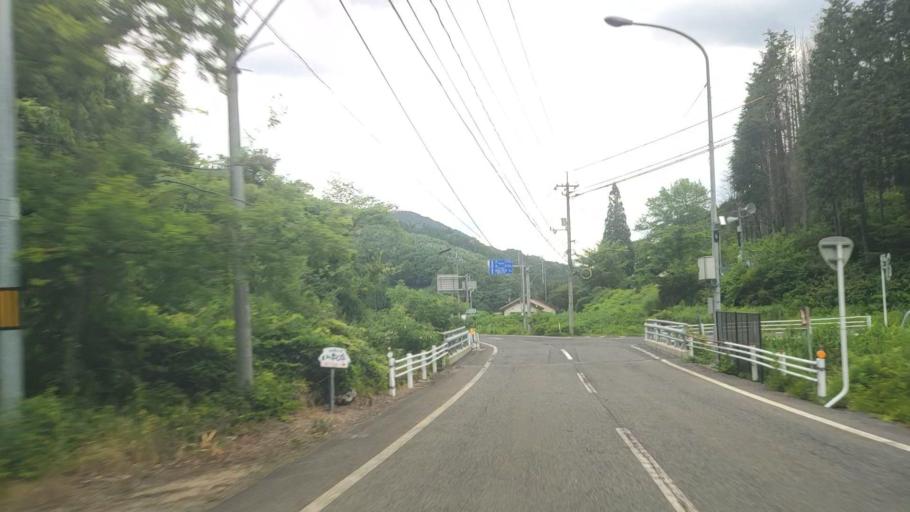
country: JP
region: Tottori
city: Kurayoshi
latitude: 35.2953
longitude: 133.9823
